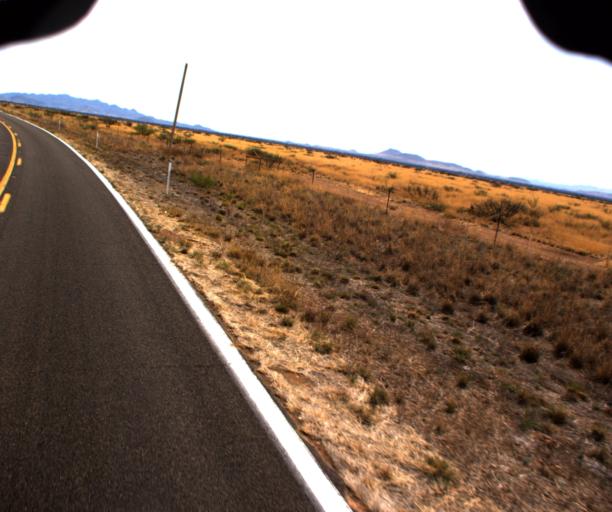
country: US
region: Arizona
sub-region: Cochise County
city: Willcox
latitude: 31.9339
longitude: -109.4914
